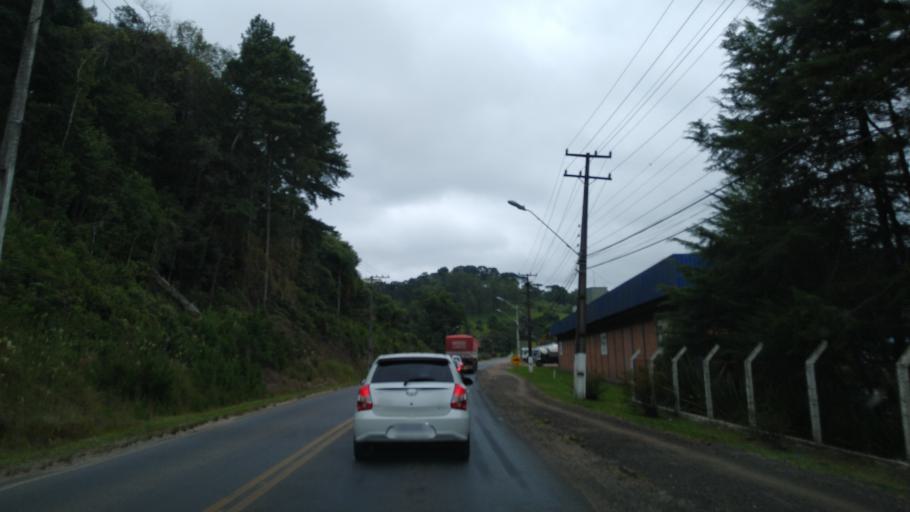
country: BR
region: Parana
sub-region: Uniao Da Vitoria
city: Uniao da Vitoria
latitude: -26.2511
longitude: -51.1140
